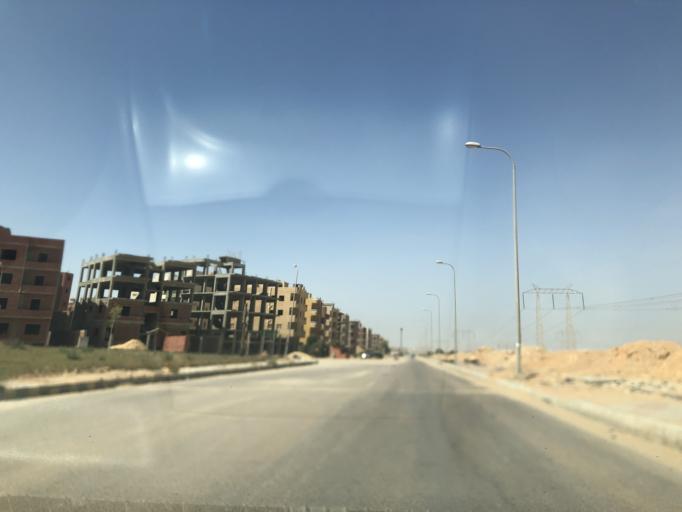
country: EG
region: Al Jizah
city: Madinat Sittah Uktubar
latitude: 29.9168
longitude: 31.0508
